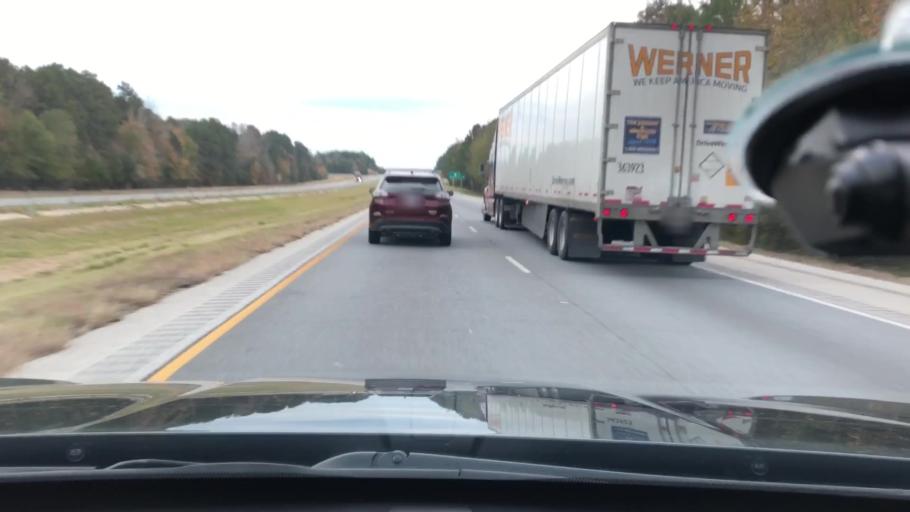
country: US
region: Arkansas
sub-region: Clark County
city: Arkadelphia
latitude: 34.0667
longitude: -93.1241
